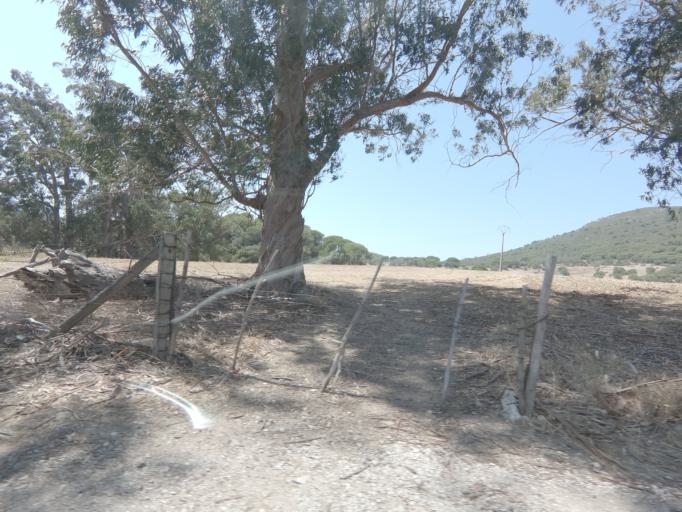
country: PT
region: Setubal
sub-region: Setubal
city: Setubal
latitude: 38.5232
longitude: -8.9317
